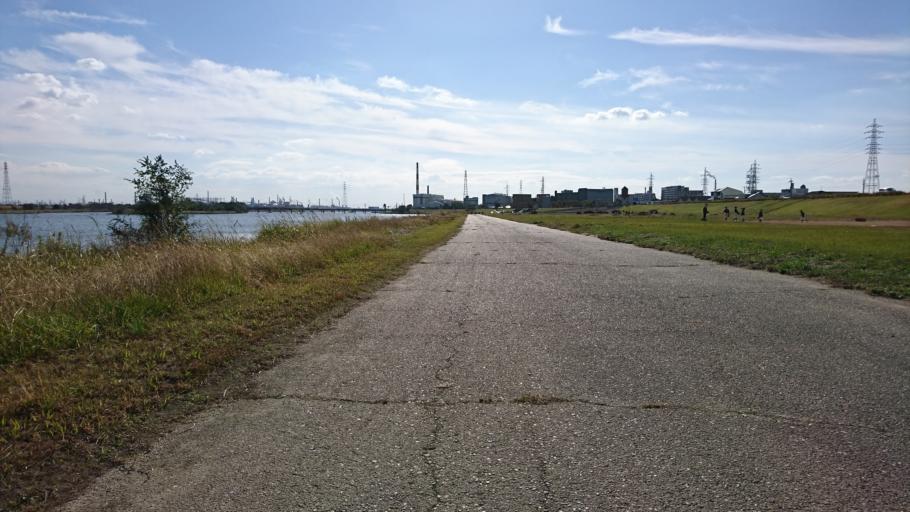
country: JP
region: Hyogo
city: Kakogawacho-honmachi
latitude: 34.7597
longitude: 134.8059
